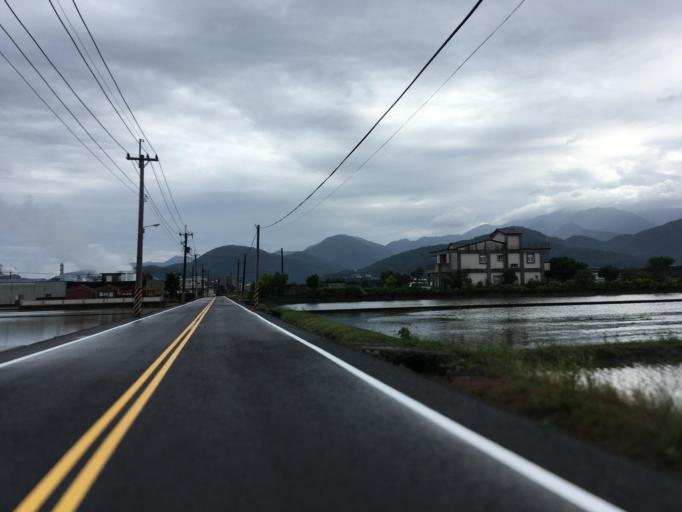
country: TW
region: Taiwan
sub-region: Yilan
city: Yilan
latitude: 24.6399
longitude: 121.8082
